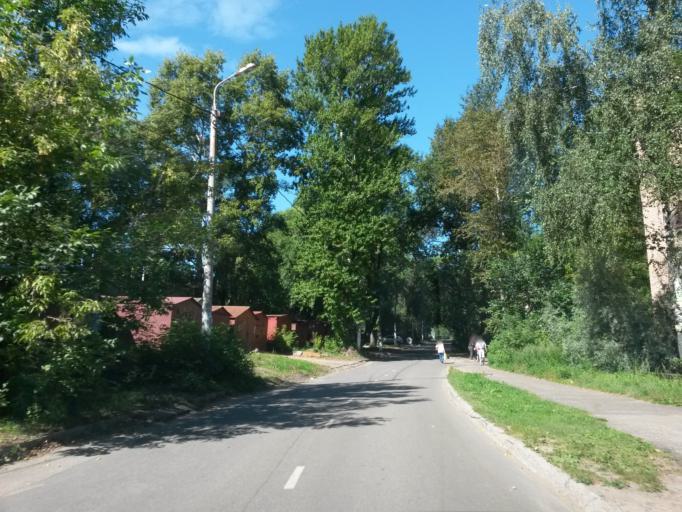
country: RU
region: Jaroslavl
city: Yaroslavl
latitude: 57.5874
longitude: 39.8634
